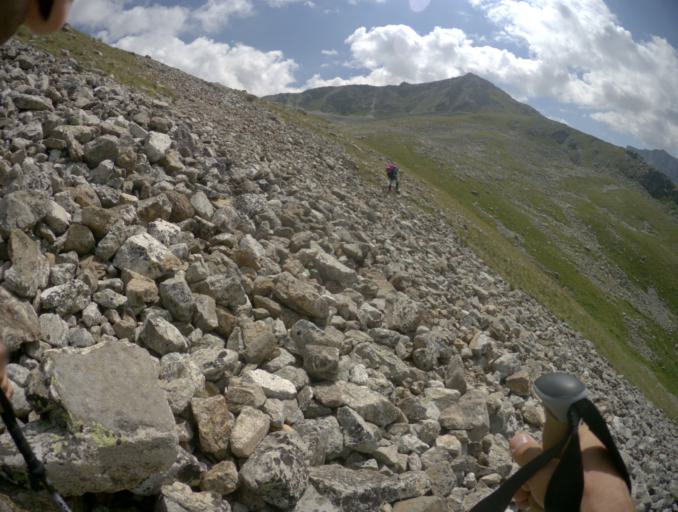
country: RU
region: Karachayevo-Cherkesiya
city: Uchkulan
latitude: 43.3010
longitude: 42.0634
